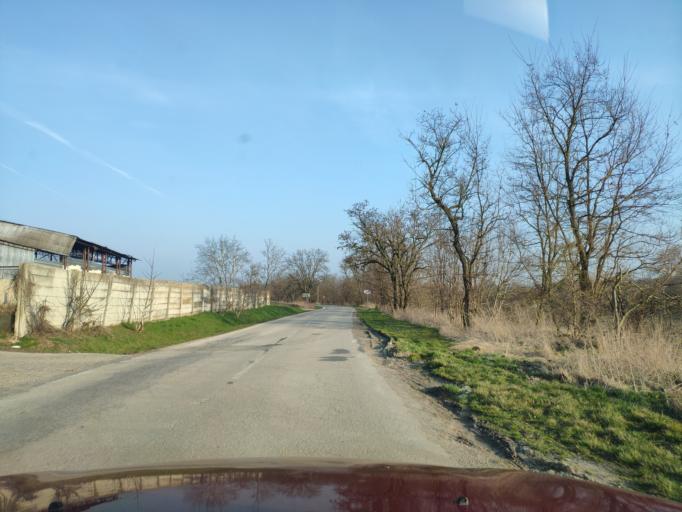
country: SK
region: Bratislavsky
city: Modra
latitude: 48.3312
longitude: 17.4059
